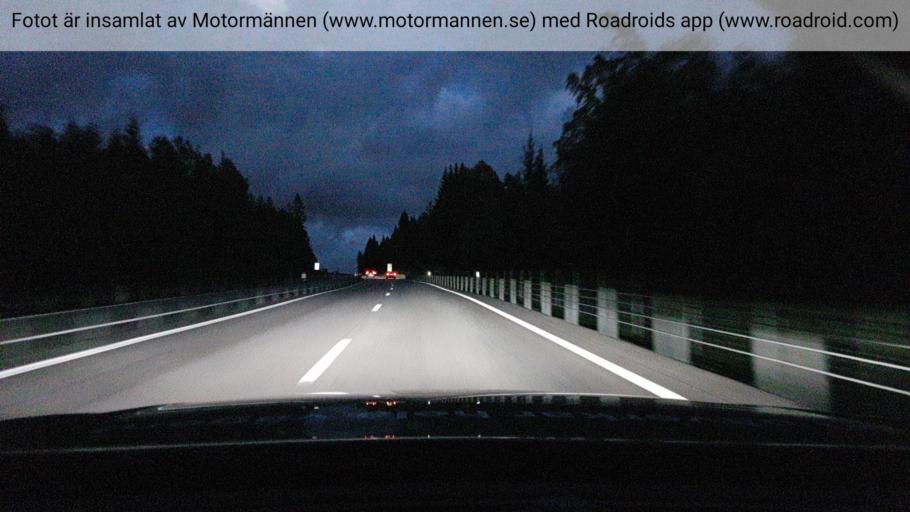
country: SE
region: Vaermland
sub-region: Kristinehamns Kommun
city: Bjorneborg
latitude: 59.3102
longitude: 14.2794
